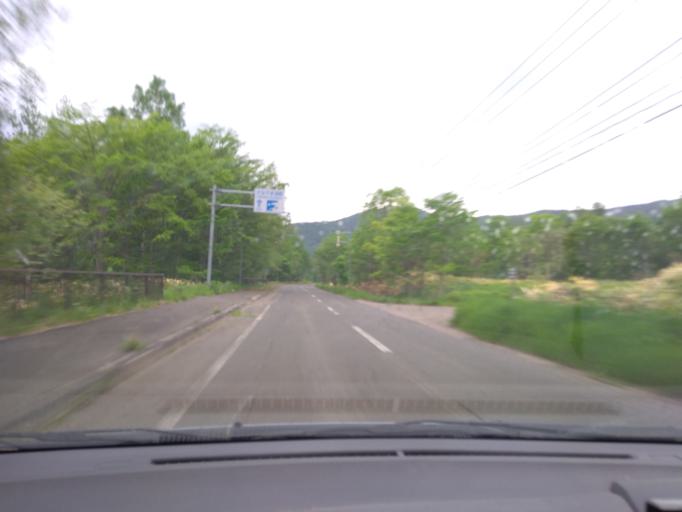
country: JP
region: Hokkaido
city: Shimo-furano
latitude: 43.1764
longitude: 142.5319
